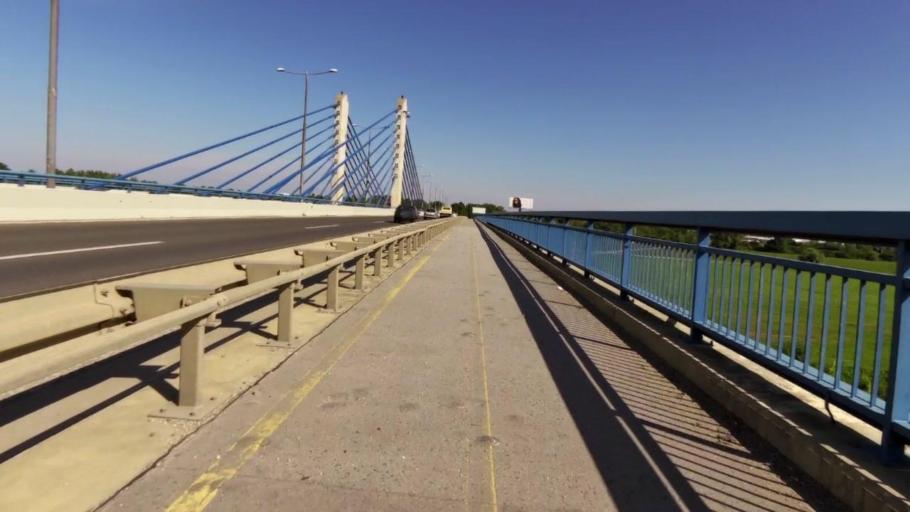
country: HR
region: Zagrebacka
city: Micevec
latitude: 45.7704
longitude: 16.0696
